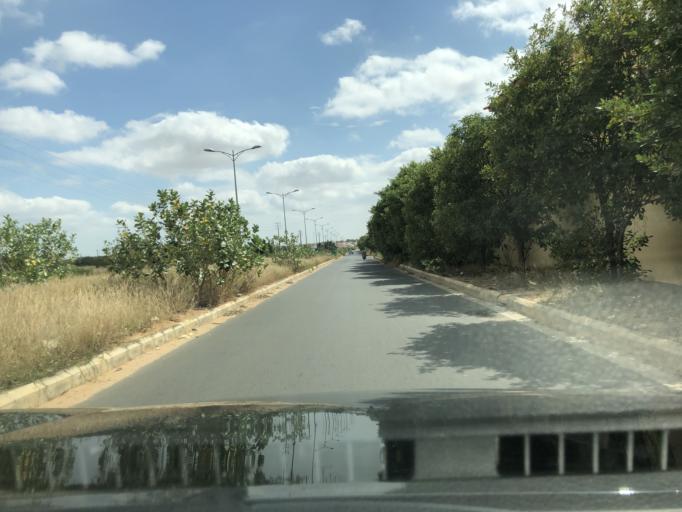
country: AO
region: Luanda
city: Luanda
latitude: -8.9488
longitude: 13.2426
